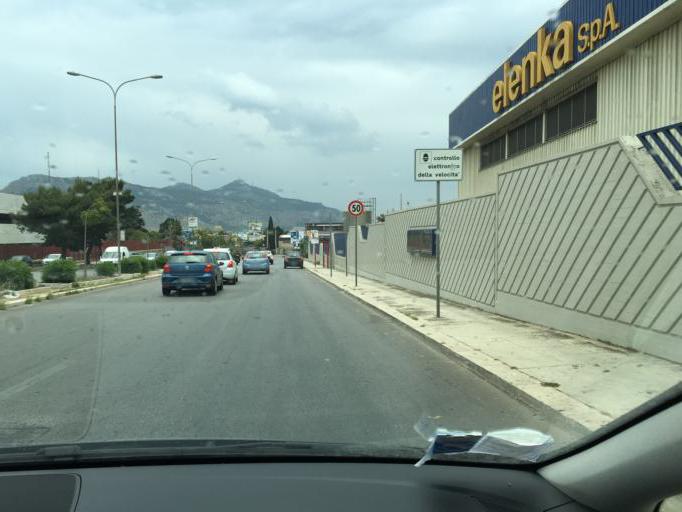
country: IT
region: Sicily
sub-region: Palermo
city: Isola delle Femmine
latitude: 38.1896
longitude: 13.2938
